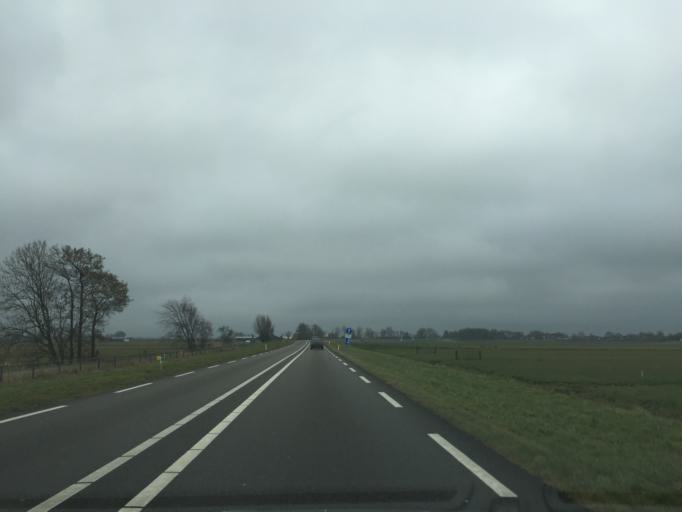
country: NL
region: South Holland
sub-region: Gemeente Kaag en Braassem
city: Leimuiden
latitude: 52.2009
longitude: 4.6793
